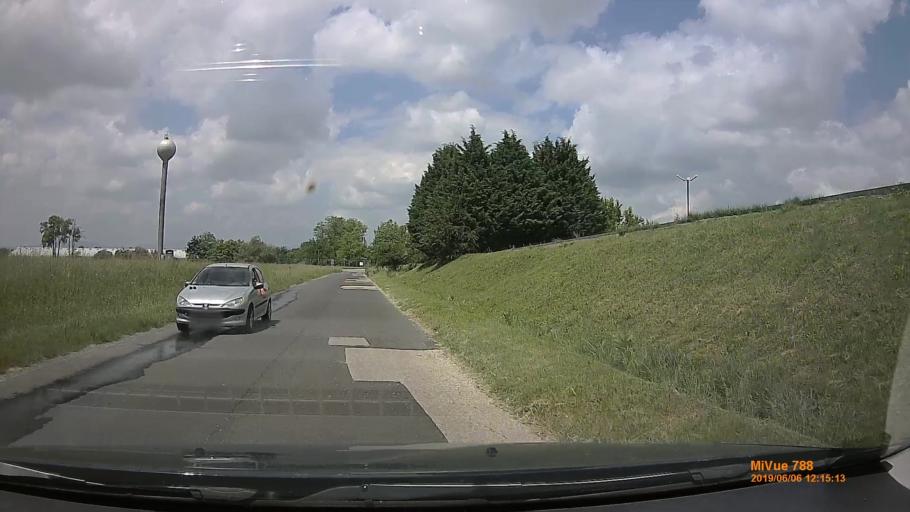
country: HU
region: Pest
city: Mogyorod
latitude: 47.5907
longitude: 19.2477
